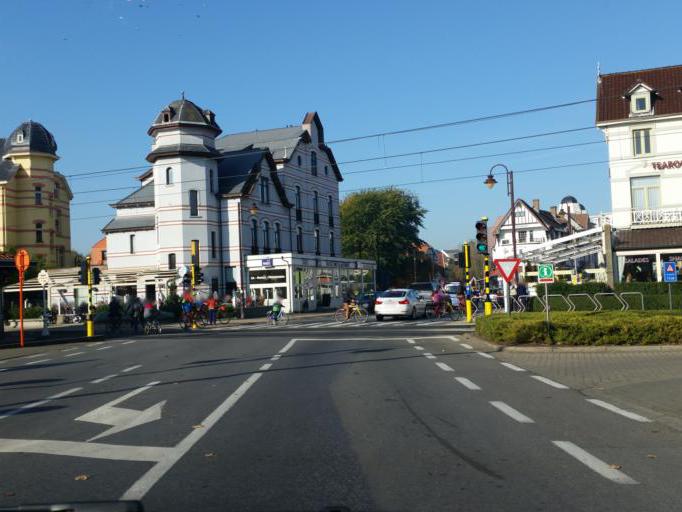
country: BE
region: Flanders
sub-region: Provincie West-Vlaanderen
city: De Haan
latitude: 51.2726
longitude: 3.0334
